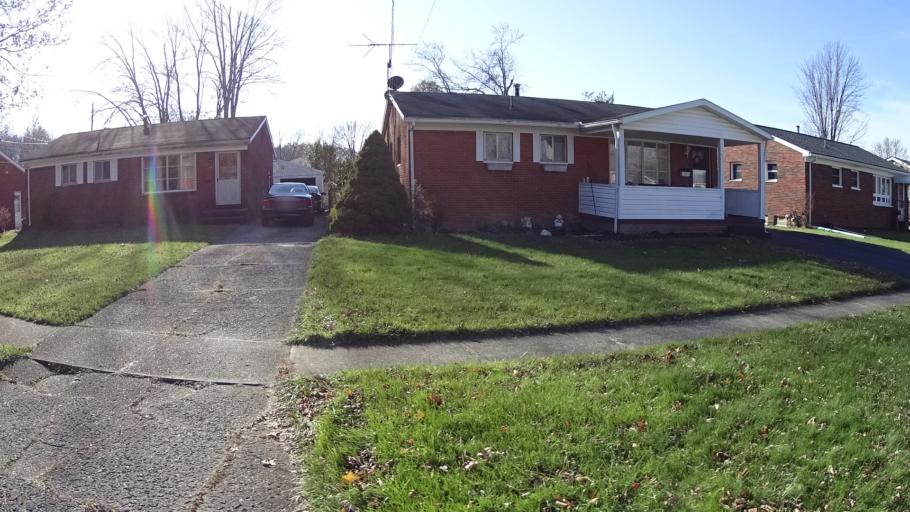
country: US
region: Ohio
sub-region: Lorain County
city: Sheffield
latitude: 41.3966
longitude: -82.0690
